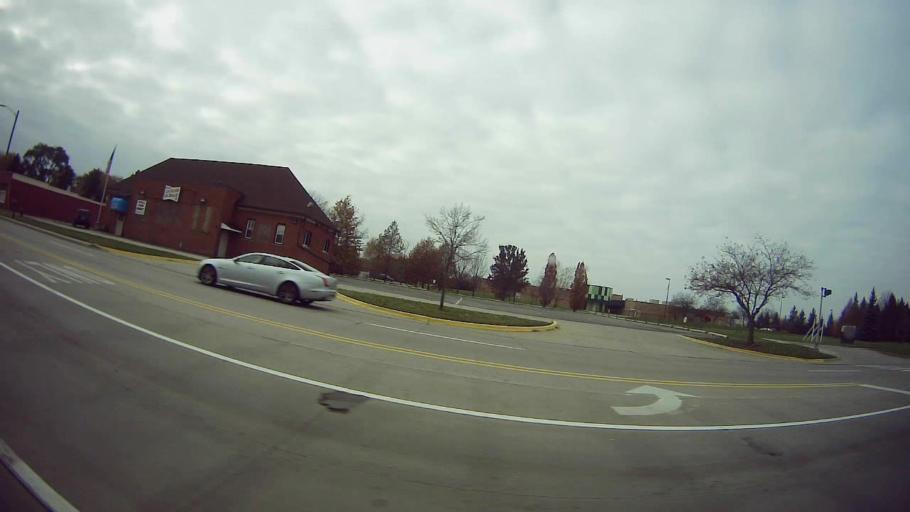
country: US
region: Michigan
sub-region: Macomb County
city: Warren
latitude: 42.4710
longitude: -83.0649
